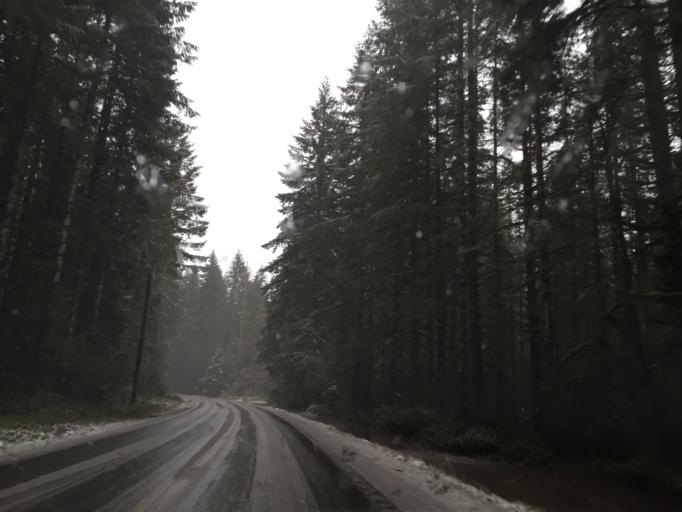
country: US
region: Washington
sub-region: Thurston County
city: Rochester
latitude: 46.9509
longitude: -123.0748
